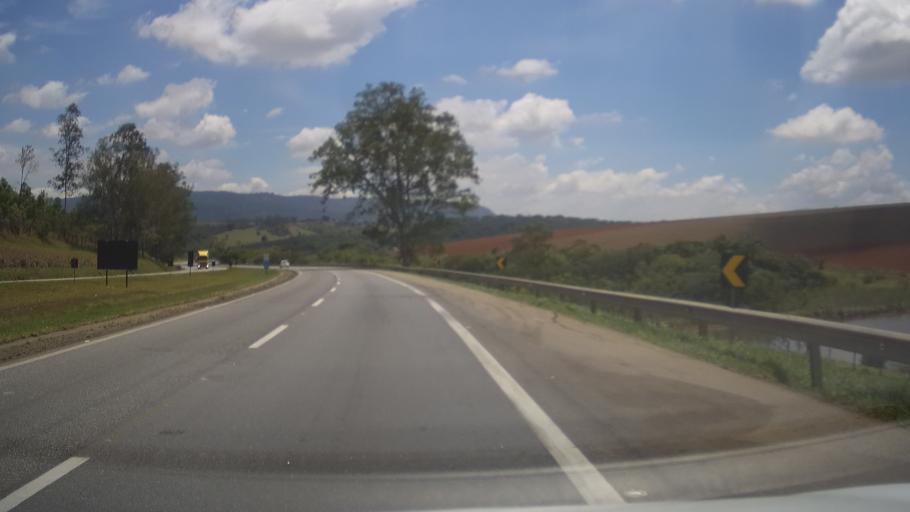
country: BR
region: Minas Gerais
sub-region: Sao Goncalo Do Sapucai
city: Sao Goncalo do Sapucai
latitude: -21.9288
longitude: -45.6114
